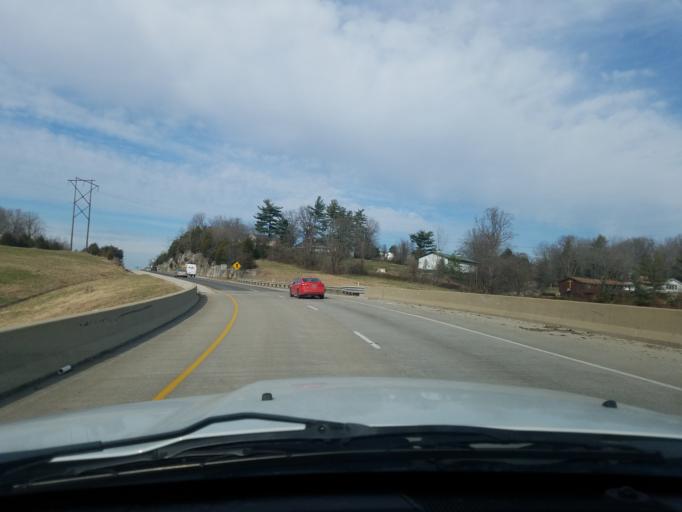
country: US
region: Indiana
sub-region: Lawrence County
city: Bedford
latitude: 38.8288
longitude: -86.5057
